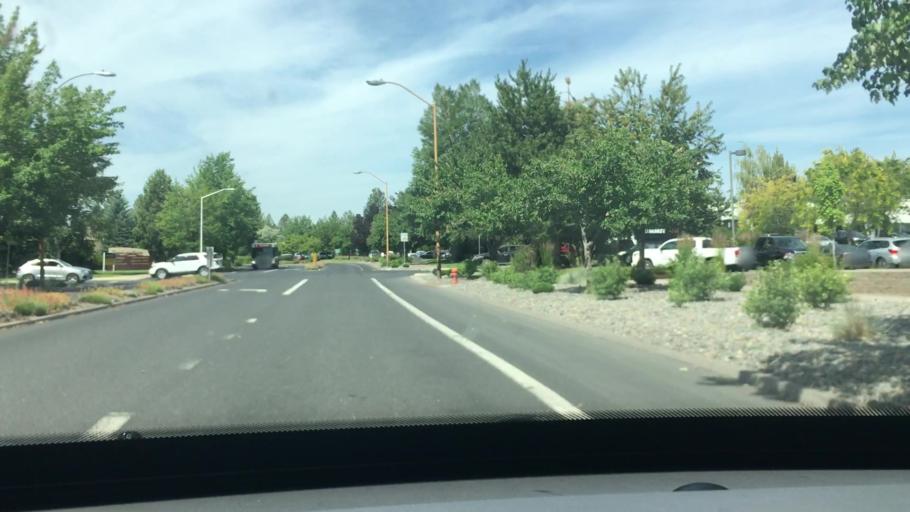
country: US
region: Oregon
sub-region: Deschutes County
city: Bend
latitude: 44.0442
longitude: -121.3246
